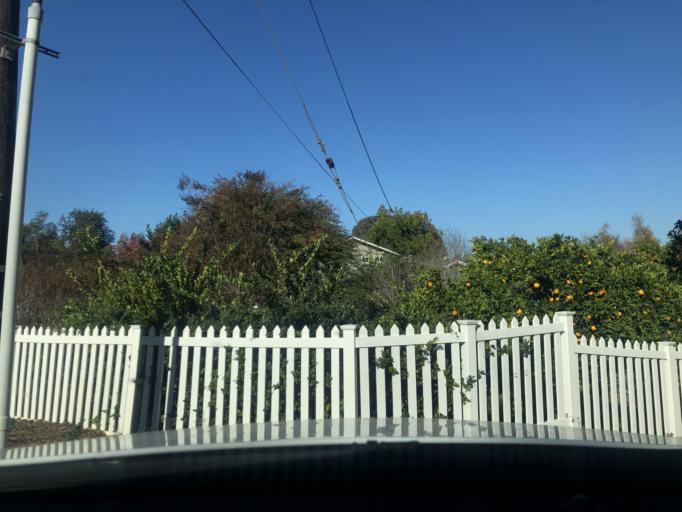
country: US
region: California
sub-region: San Diego County
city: Rancho San Diego
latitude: 32.7751
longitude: -116.9403
